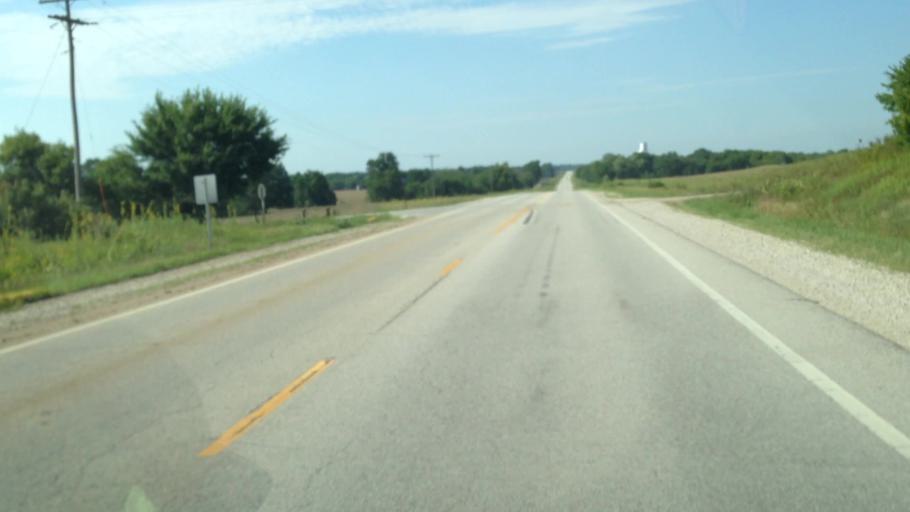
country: US
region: Kansas
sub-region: Neosho County
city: Erie
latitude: 37.4997
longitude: -95.2696
